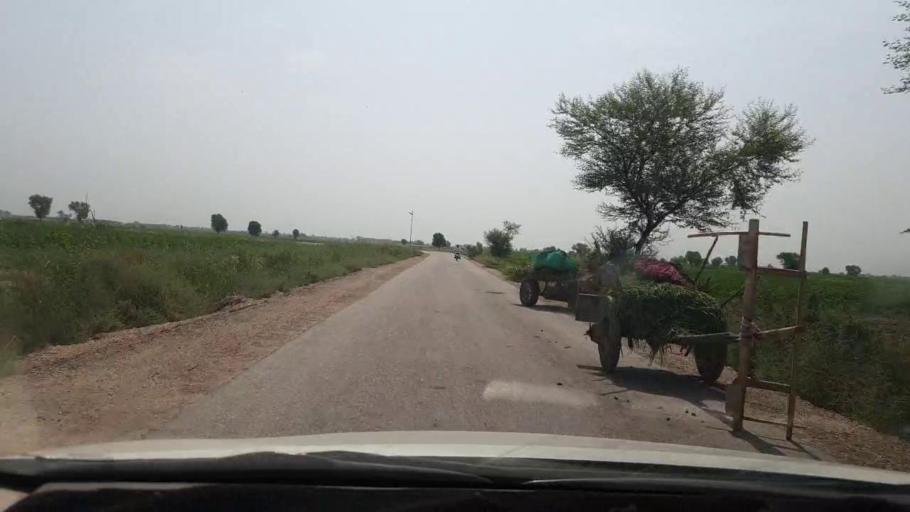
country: PK
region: Sindh
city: Rohri
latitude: 27.5376
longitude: 69.0026
